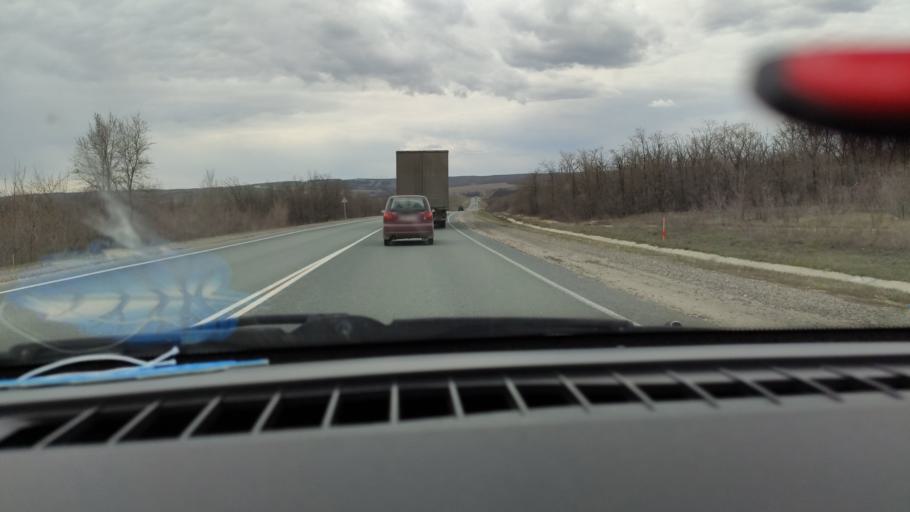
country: RU
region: Saratov
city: Sinodskoye
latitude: 51.9322
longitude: 46.5827
